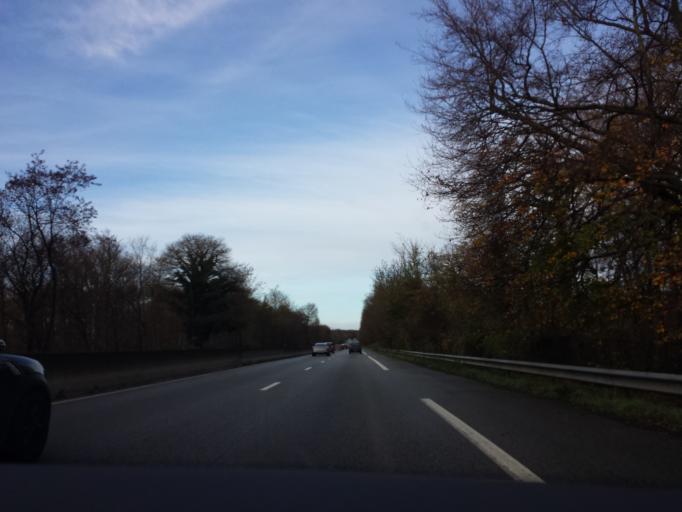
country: FR
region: Ile-de-France
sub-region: Departement des Yvelines
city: Noisy-le-Roi
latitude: 48.8597
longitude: 2.0491
